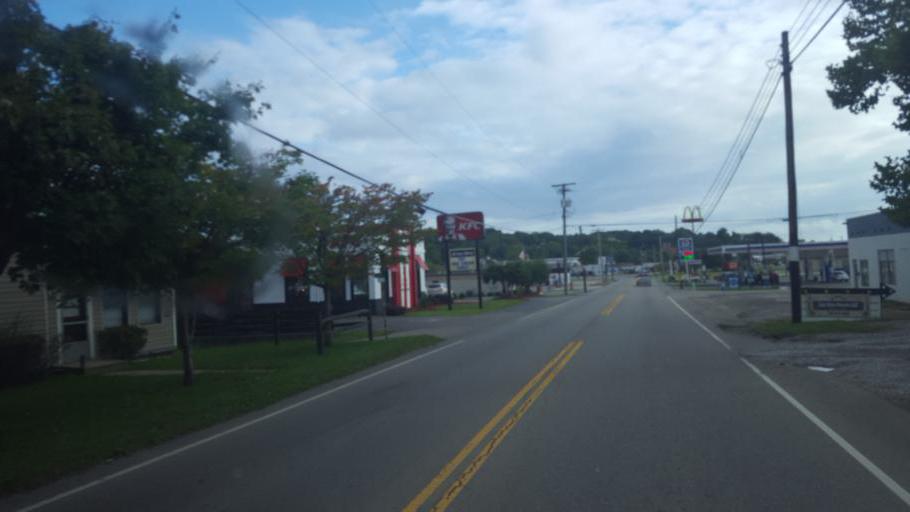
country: US
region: Ohio
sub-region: Jackson County
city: Oak Hill
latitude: 38.9019
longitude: -82.5690
